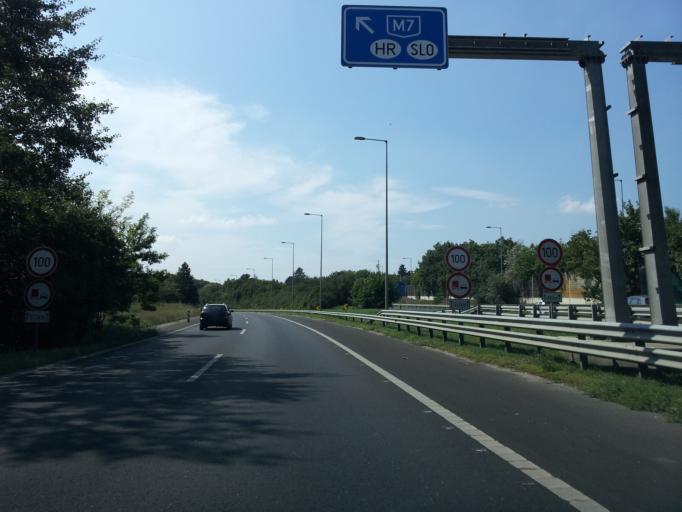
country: HU
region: Pest
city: Toeroekbalint
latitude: 47.4526
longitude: 18.9213
